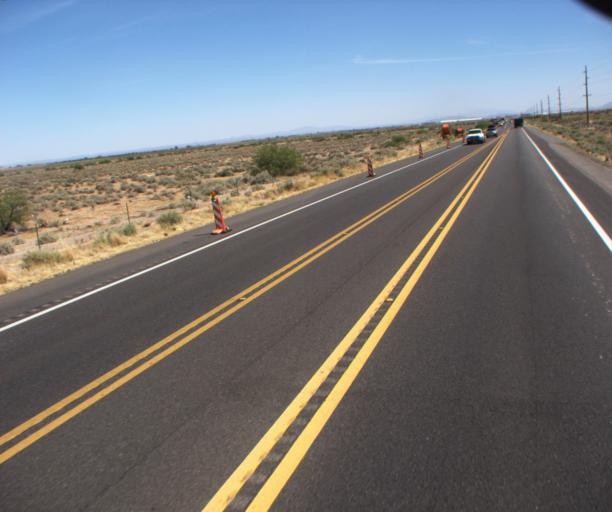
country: US
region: Arizona
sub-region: Pinal County
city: Blackwater
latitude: 33.0200
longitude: -111.6340
